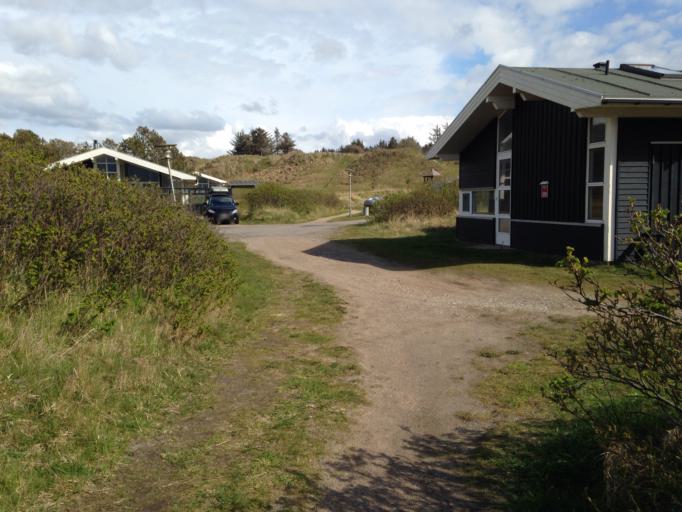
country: DK
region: North Denmark
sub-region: Hjorring Kommune
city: Hjorring
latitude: 57.4907
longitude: 9.8358
